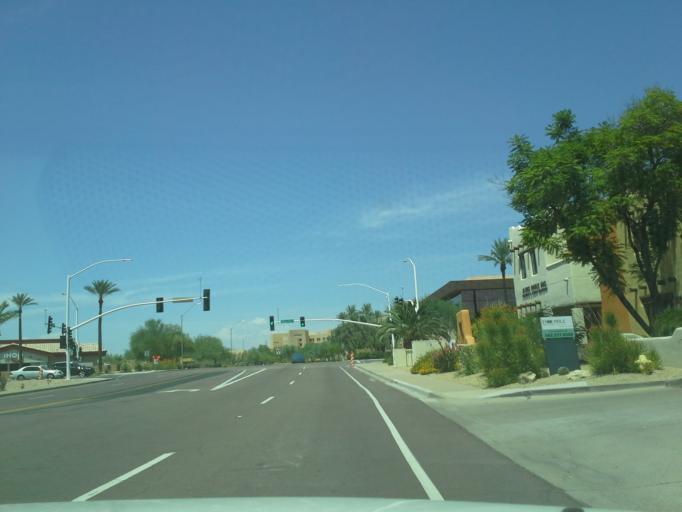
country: US
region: Arizona
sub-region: Maricopa County
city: Scottsdale
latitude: 33.5744
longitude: -111.8861
